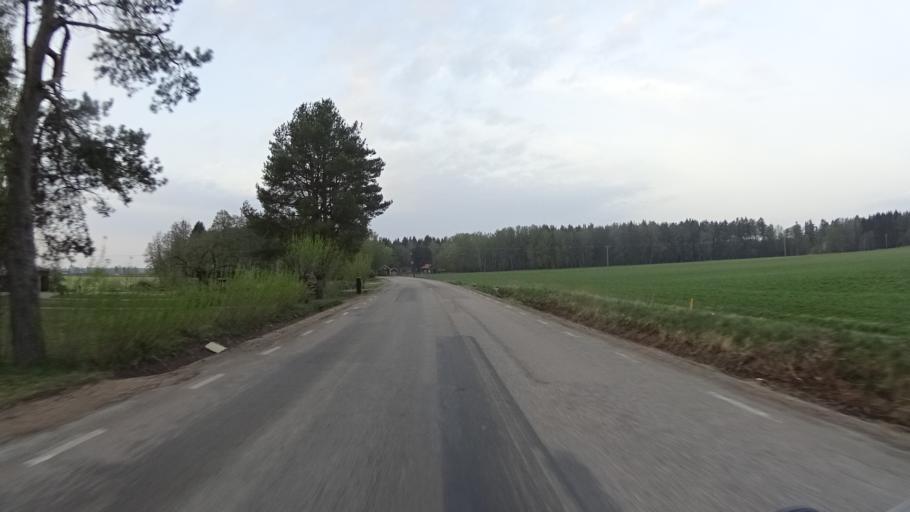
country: SE
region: Vaestra Goetaland
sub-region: Gotene Kommun
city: Kallby
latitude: 58.4887
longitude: 13.3151
